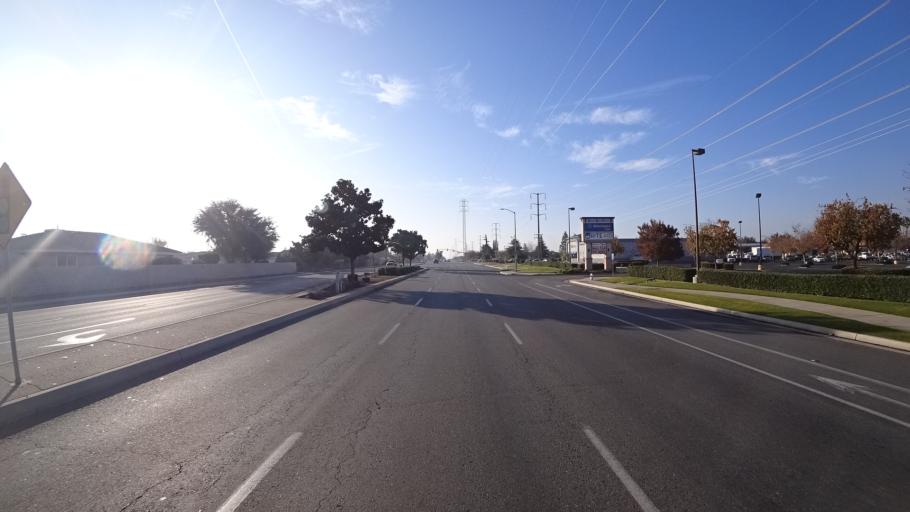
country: US
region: California
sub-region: Kern County
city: Greenacres
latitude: 35.4141
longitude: -119.0923
